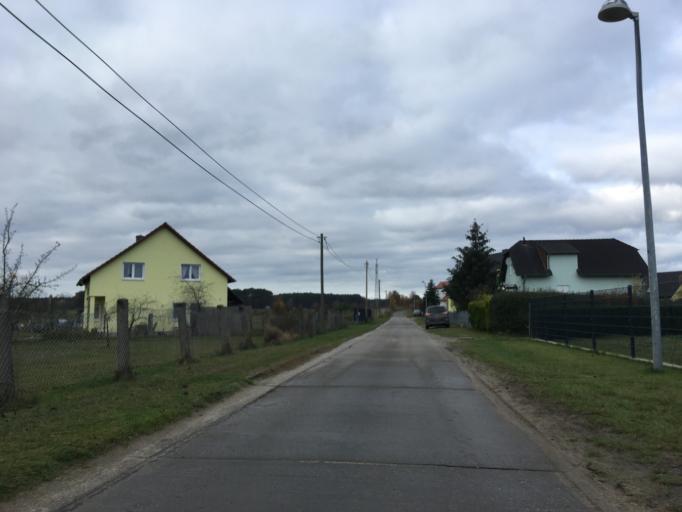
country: DE
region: Brandenburg
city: Schenkendobern
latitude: 51.9824
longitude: 14.5312
